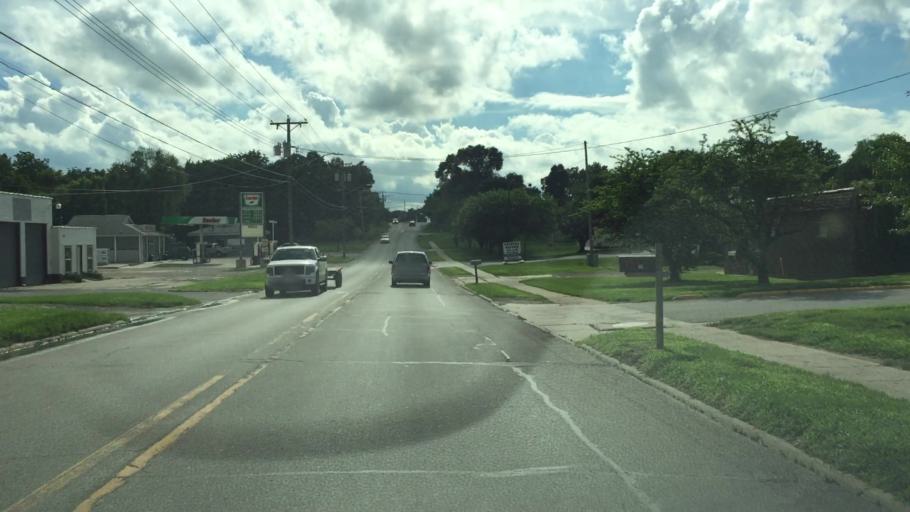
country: US
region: Iowa
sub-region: Jasper County
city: Newton
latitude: 41.6993
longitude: -93.0702
